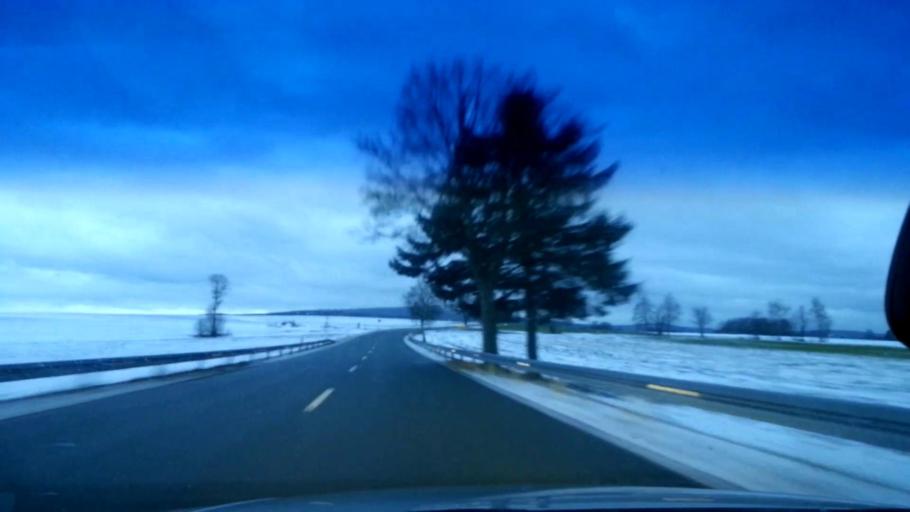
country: DE
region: Bavaria
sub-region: Upper Franconia
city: Weissenstadt
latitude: 50.1141
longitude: 11.8987
